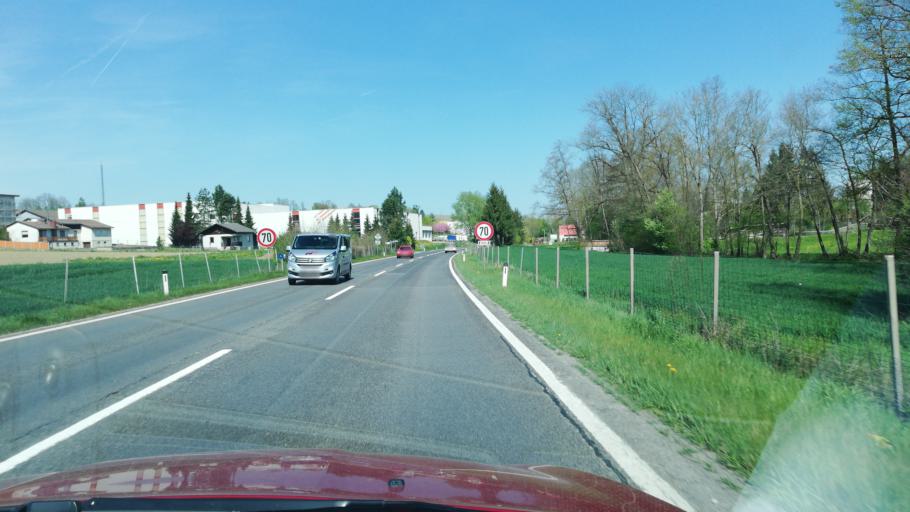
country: AT
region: Upper Austria
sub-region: Wels-Land
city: Thalheim bei Wels
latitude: 48.1352
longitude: 14.0485
